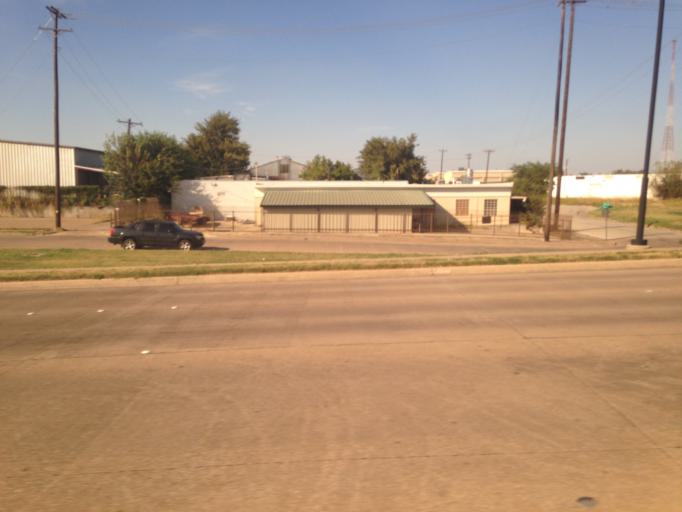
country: US
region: Texas
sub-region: Tarrant County
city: Fort Worth
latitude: 32.7060
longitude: -97.3261
